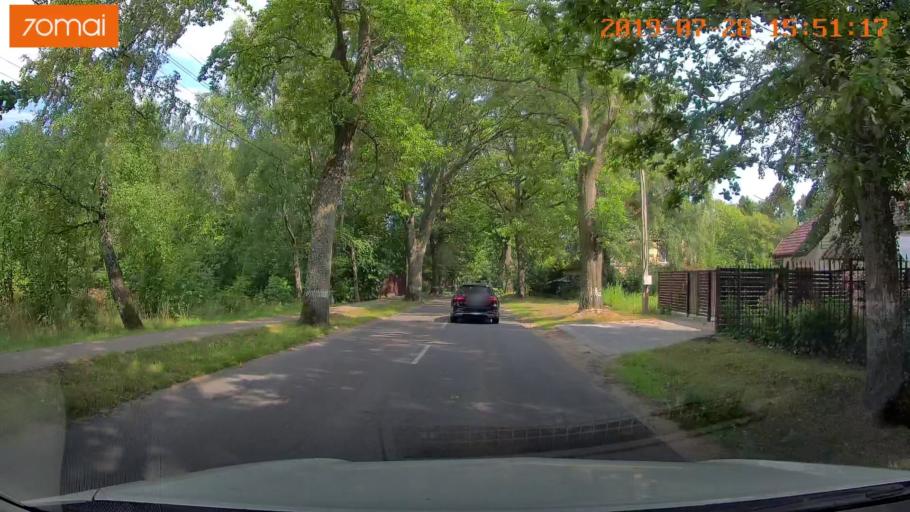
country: RU
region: Kaliningrad
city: Otradnoye
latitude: 54.9414
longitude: 20.1032
